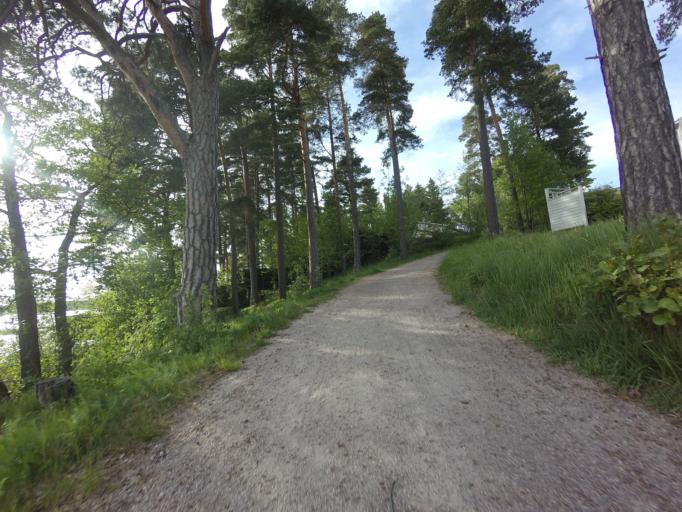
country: FI
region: Uusimaa
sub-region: Helsinki
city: Koukkuniemi
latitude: 60.1451
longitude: 24.7336
